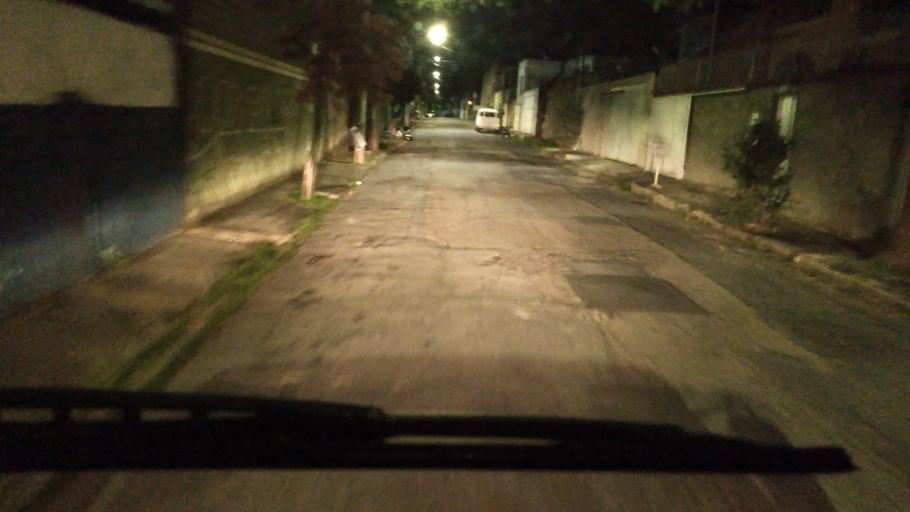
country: BR
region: Minas Gerais
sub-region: Belo Horizonte
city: Belo Horizonte
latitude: -19.9104
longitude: -43.9630
